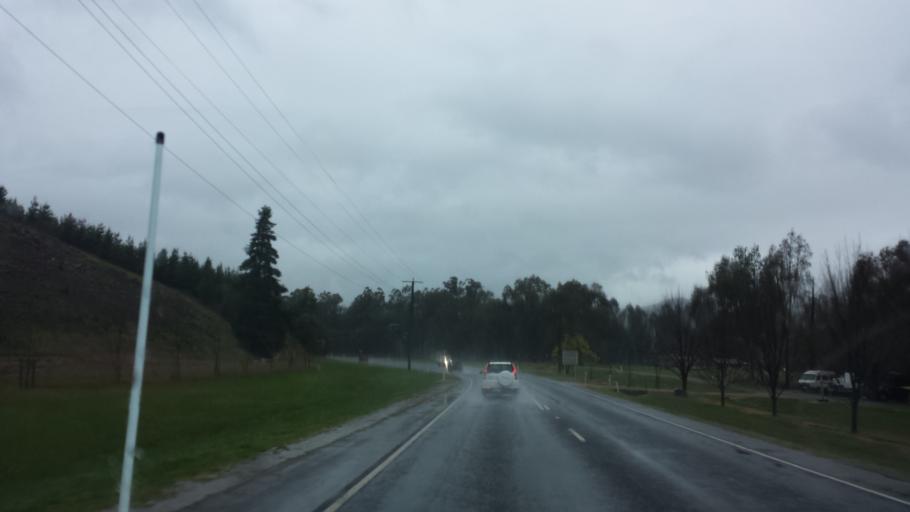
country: AU
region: Victoria
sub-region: Alpine
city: Mount Beauty
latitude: -36.5797
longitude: 146.7502
